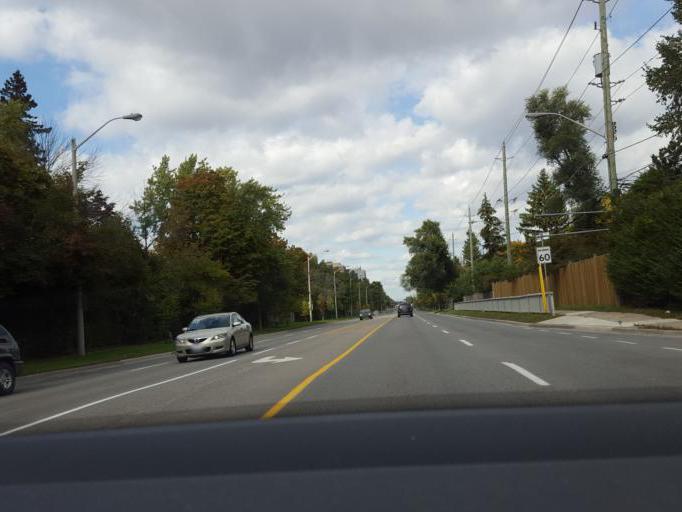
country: CA
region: Ontario
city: Willowdale
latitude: 43.7465
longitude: -79.3586
